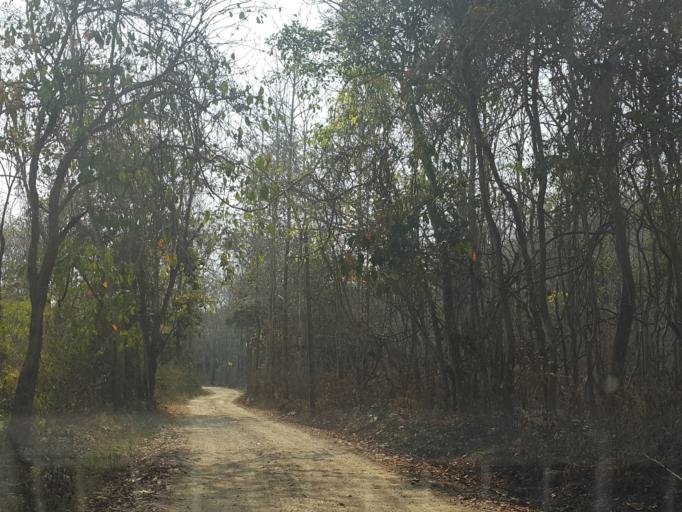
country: TH
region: Chiang Mai
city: Hang Dong
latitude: 18.7109
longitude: 98.8534
